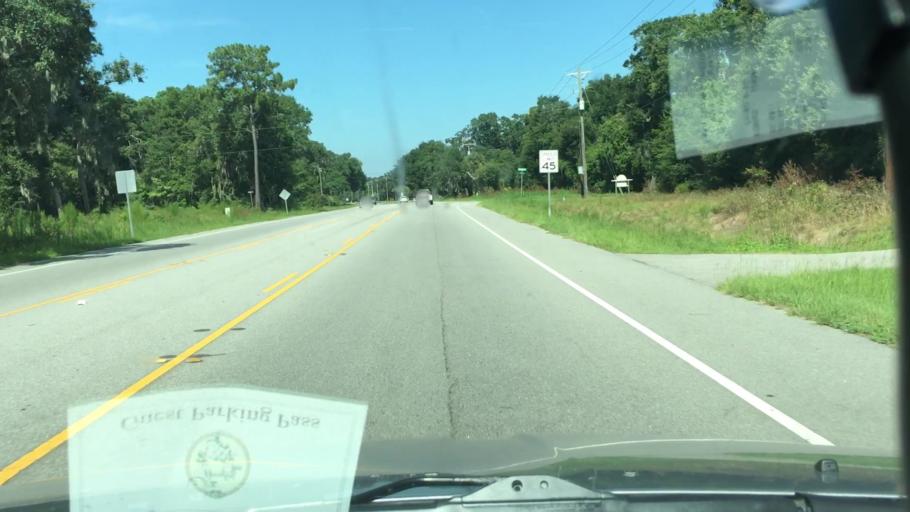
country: US
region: South Carolina
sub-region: Beaufort County
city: Beaufort
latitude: 32.4003
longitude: -80.5574
